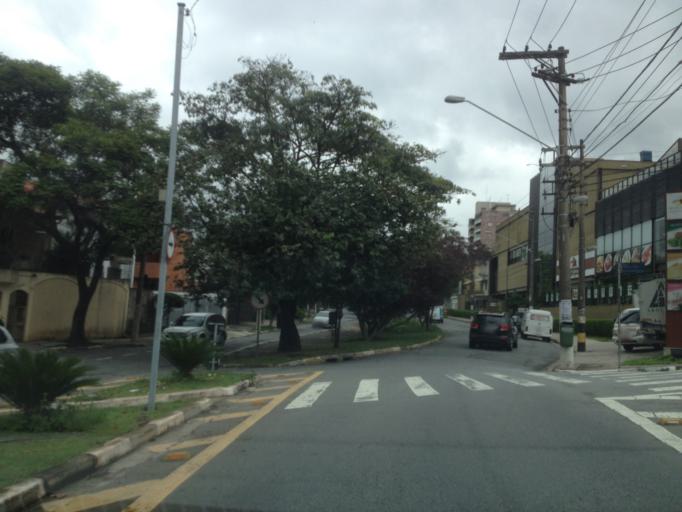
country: BR
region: Sao Paulo
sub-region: Sao Paulo
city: Sao Paulo
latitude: -23.5474
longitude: -46.6957
